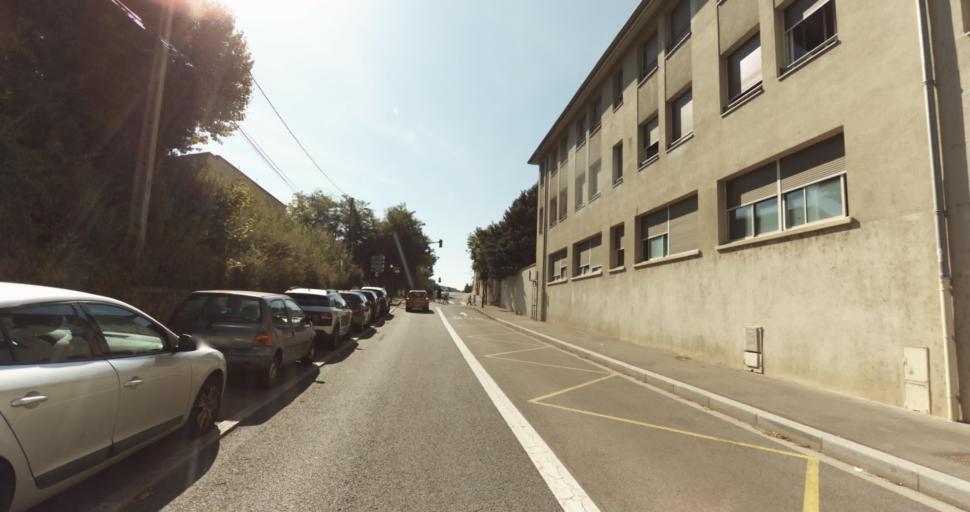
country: FR
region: Rhone-Alpes
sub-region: Departement du Rhone
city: Fleurieu-sur-Saone
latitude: 45.8703
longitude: 4.8421
